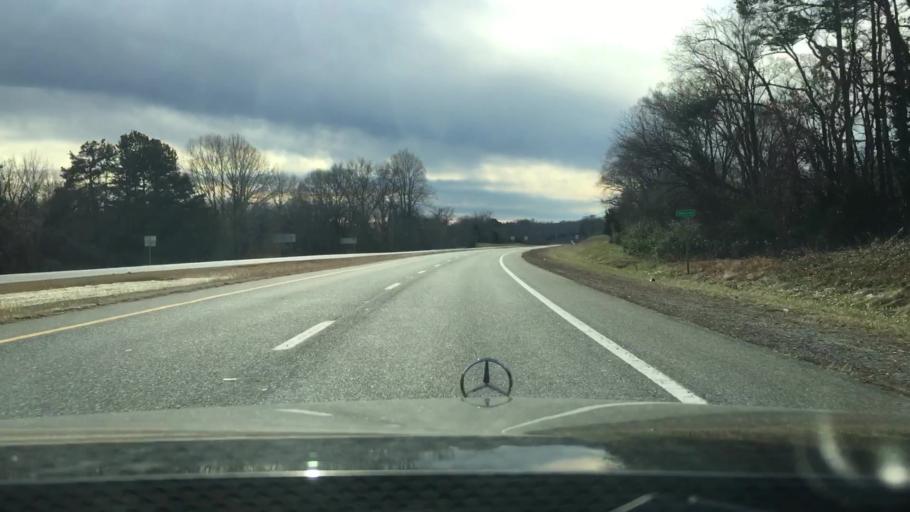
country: US
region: Virginia
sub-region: Pittsylvania County
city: Motley
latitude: 37.0641
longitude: -79.3429
